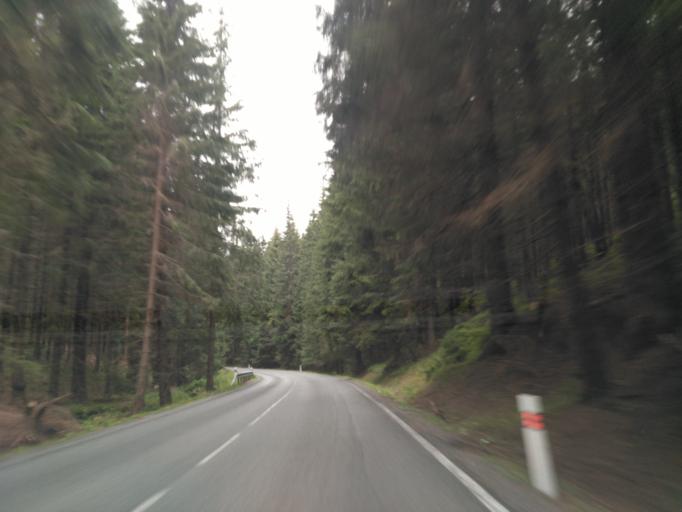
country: DE
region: Saxony
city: Johanngeorgenstadt
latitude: 50.4123
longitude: 12.7363
